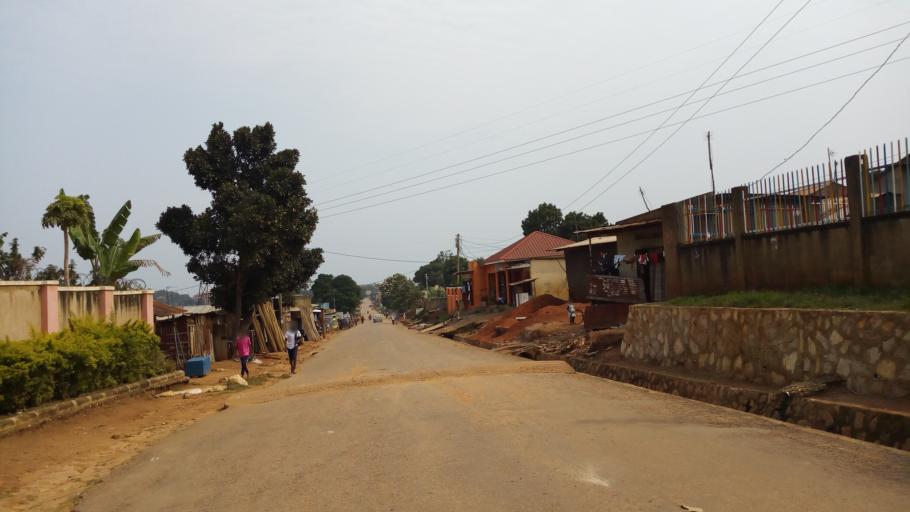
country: UG
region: Central Region
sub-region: Wakiso District
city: Kireka
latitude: 0.3085
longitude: 32.6530
